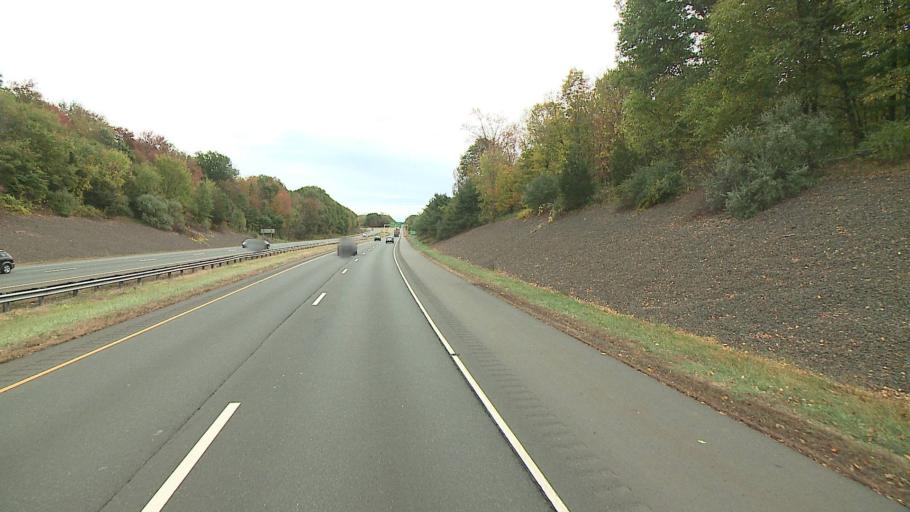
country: US
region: Connecticut
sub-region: Hartford County
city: Kensington
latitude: 41.6255
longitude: -72.7132
